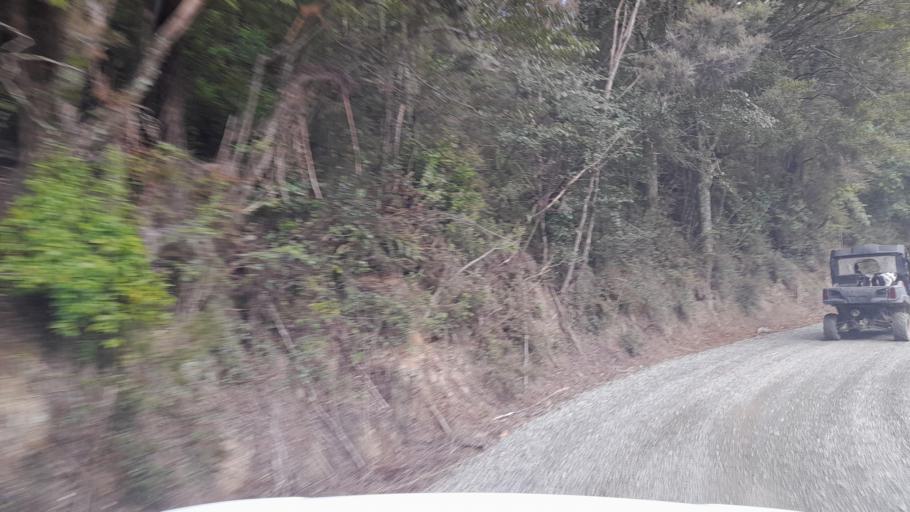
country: NZ
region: Northland
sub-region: Far North District
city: Waimate North
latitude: -35.1330
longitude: 173.7180
